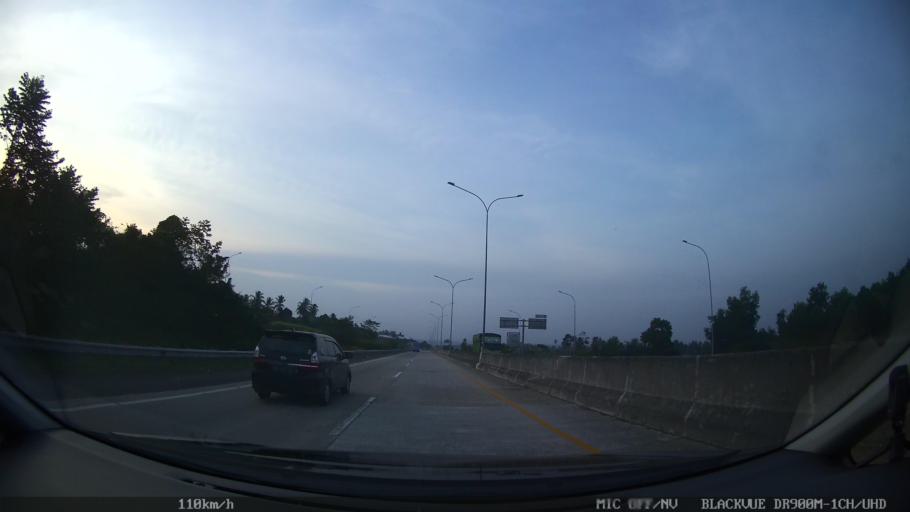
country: ID
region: Lampung
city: Penengahan
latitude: -5.8054
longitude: 105.7321
